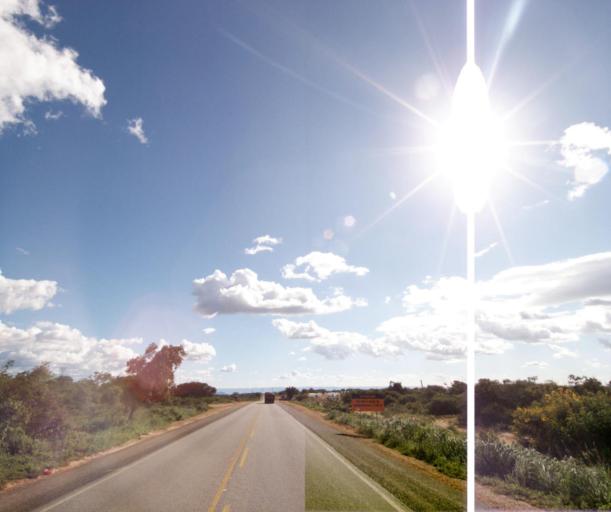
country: BR
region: Bahia
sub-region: Guanambi
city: Guanambi
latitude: -14.1347
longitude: -42.6359
